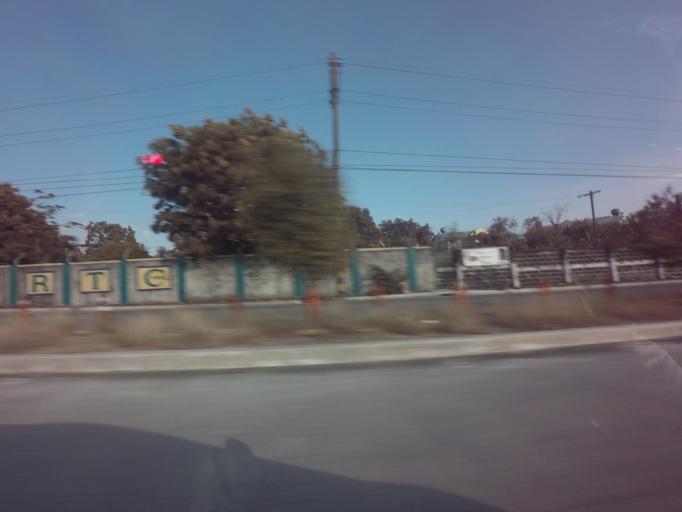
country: PH
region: Metro Manila
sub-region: Makati City
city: Makati City
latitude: 14.5076
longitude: 121.0269
